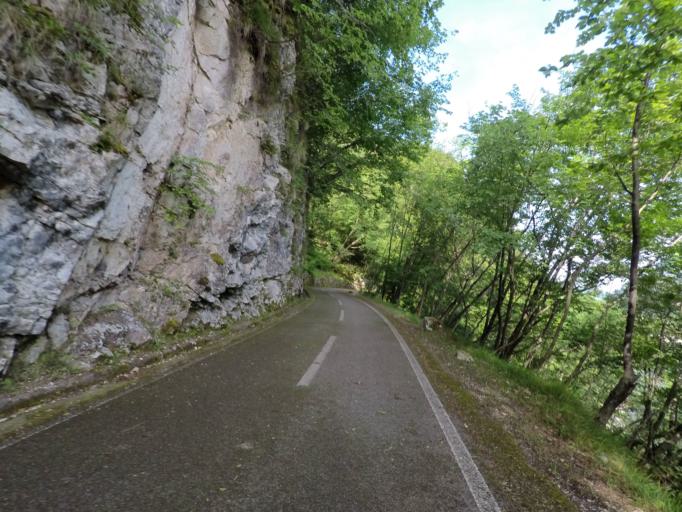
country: IT
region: Friuli Venezia Giulia
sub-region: Provincia di Udine
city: Amaro
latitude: 46.3596
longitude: 13.1088
